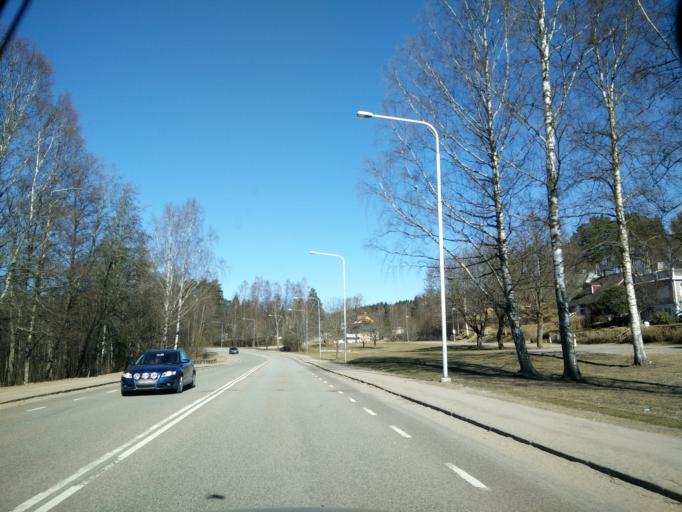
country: SE
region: Vaermland
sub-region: Hagfors Kommun
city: Hagfors
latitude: 60.0239
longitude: 13.6982
